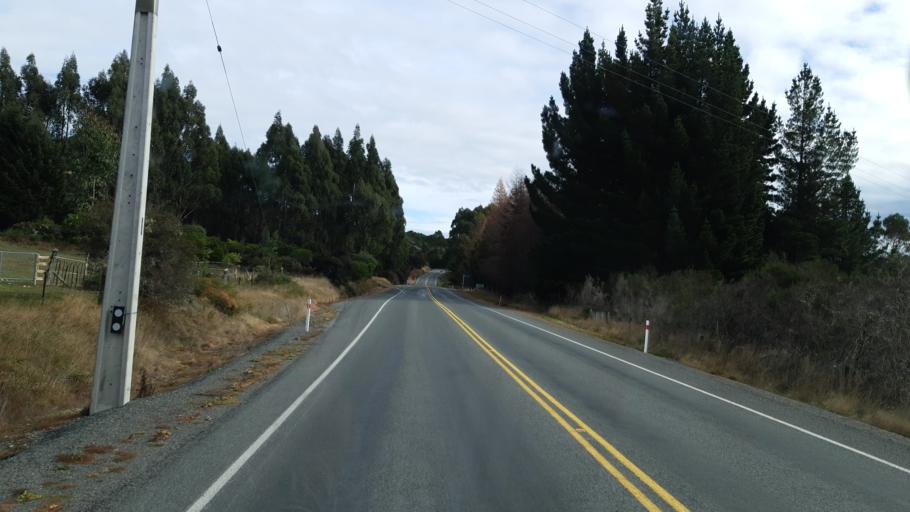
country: NZ
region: Tasman
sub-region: Tasman District
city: Wakefield
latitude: -41.7769
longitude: 172.9211
